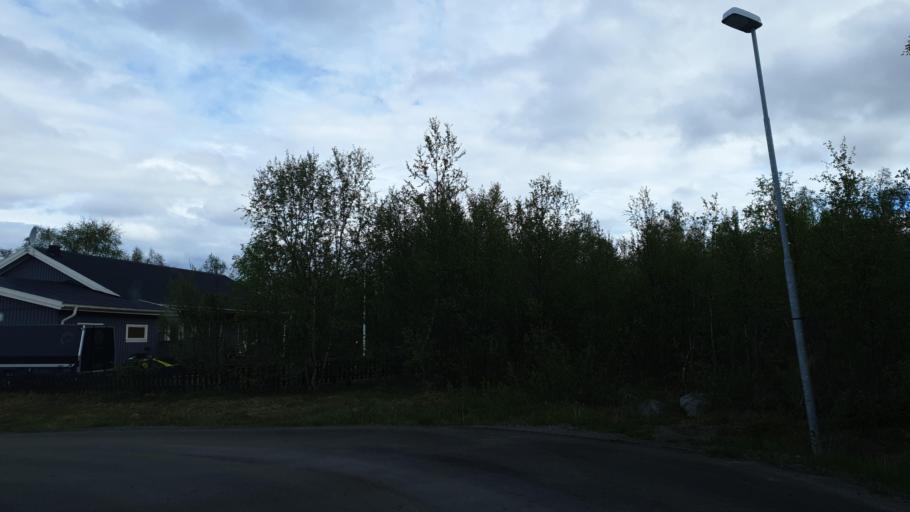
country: NO
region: Troms
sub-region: Bardu
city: Setermoen
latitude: 68.3477
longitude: 18.8334
